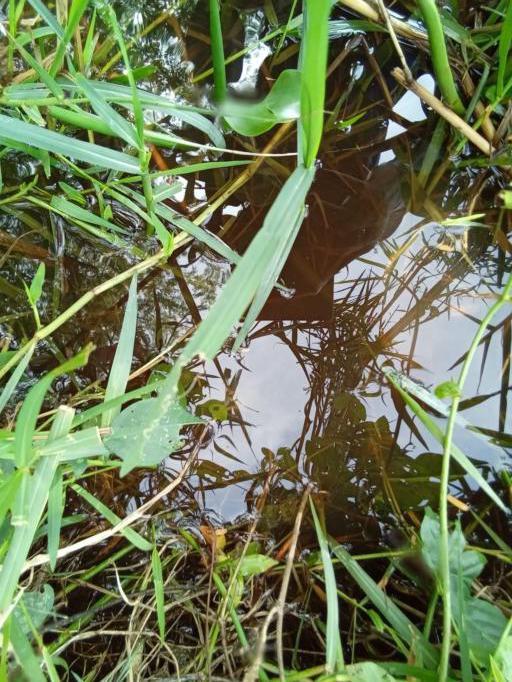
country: KE
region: Homa Bay
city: Homa Bay
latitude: -0.4589
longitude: 34.1914
